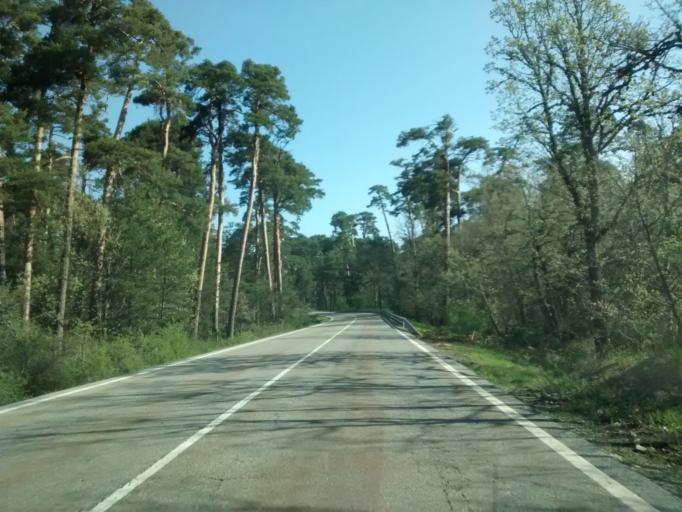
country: ES
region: Castille and Leon
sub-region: Provincia de Segovia
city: San Ildefonso
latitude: 40.8578
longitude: -4.0264
